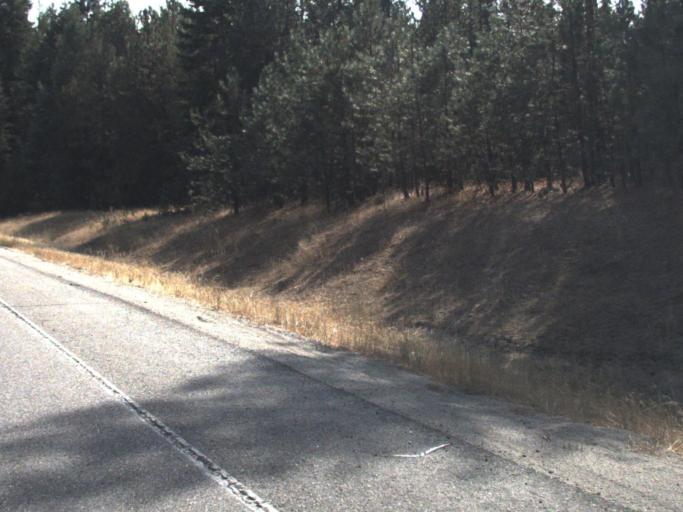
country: US
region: Washington
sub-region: Stevens County
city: Chewelah
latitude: 48.1481
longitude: -117.6860
